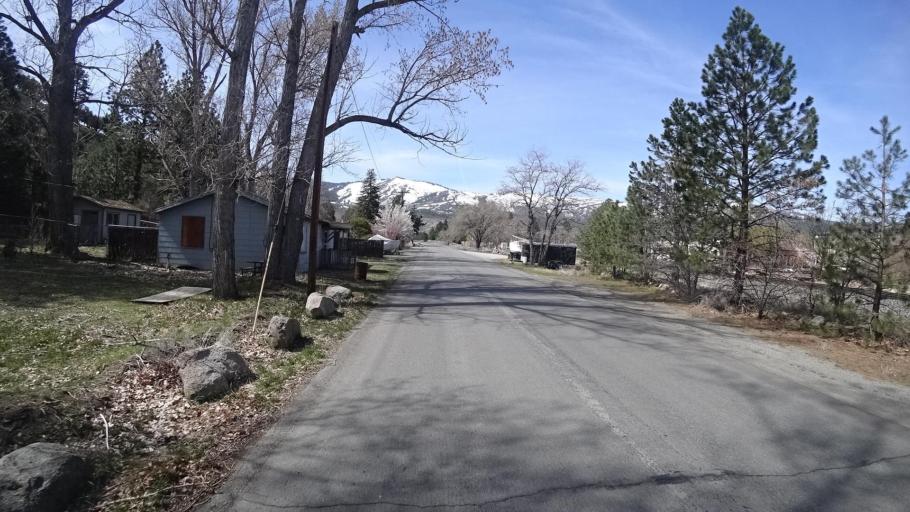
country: US
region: Nevada
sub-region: Washoe County
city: Verdi
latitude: 39.5178
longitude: -119.9872
